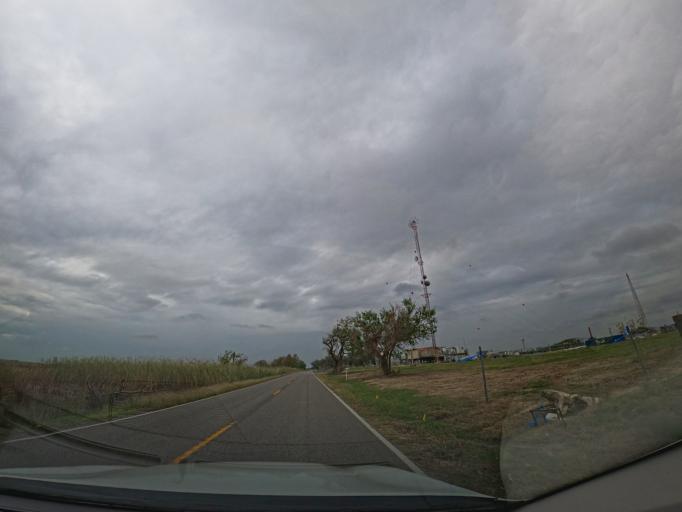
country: US
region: Louisiana
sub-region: Cameron Parish
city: Cameron
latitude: 29.7637
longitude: -92.9583
